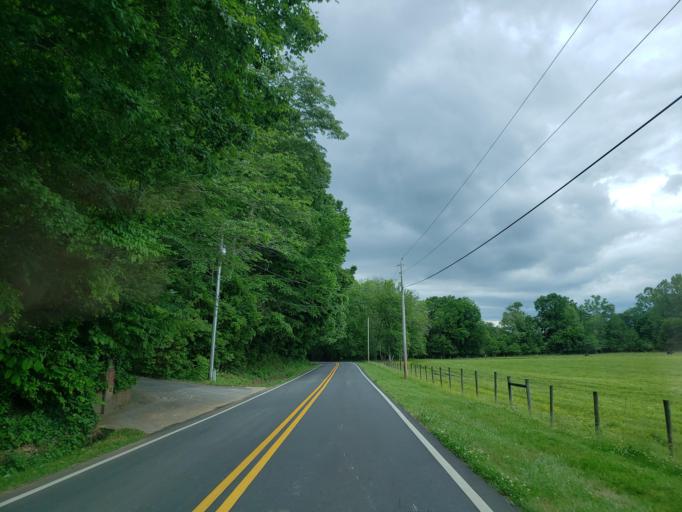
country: US
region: Georgia
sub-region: Bartow County
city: Emerson
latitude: 34.1016
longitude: -84.7747
